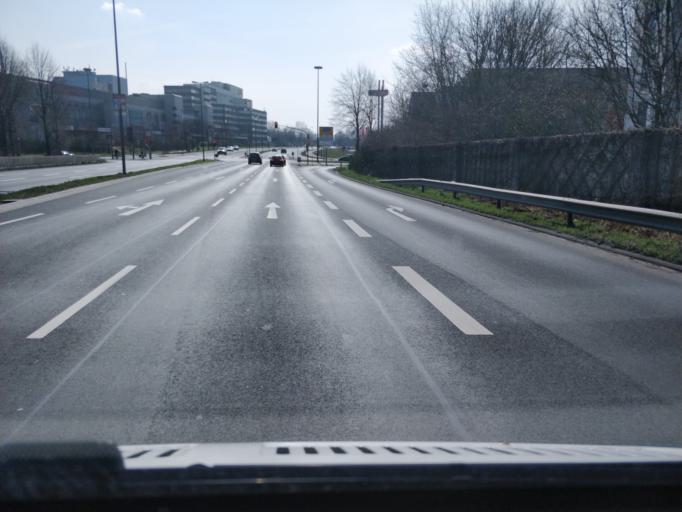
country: DE
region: North Rhine-Westphalia
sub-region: Regierungsbezirk Dusseldorf
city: Neuss
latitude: 51.2037
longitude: 6.7156
